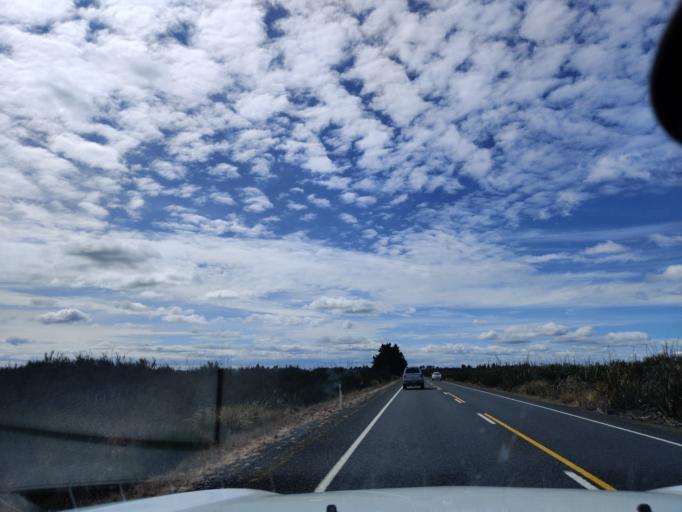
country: NZ
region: Manawatu-Wanganui
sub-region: Ruapehu District
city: Waiouru
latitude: -39.1852
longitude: 175.4021
